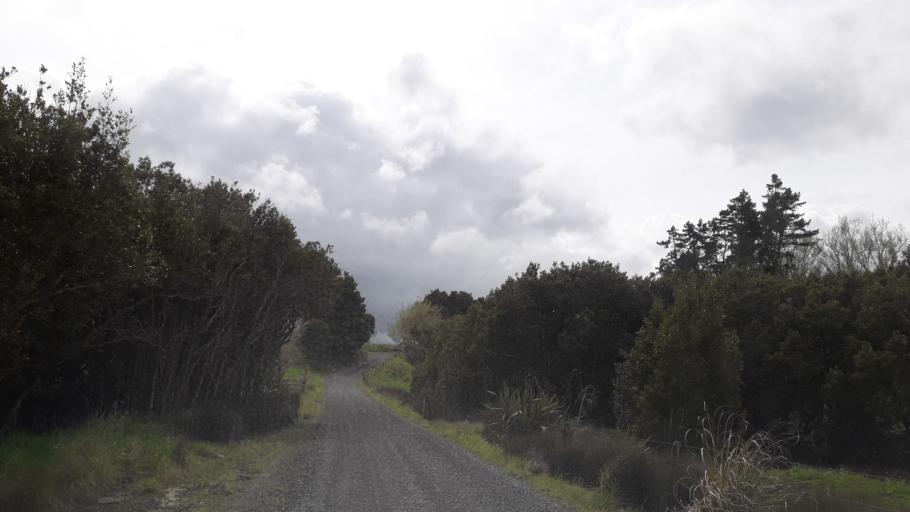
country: NZ
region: Northland
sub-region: Far North District
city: Waimate North
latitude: -35.3023
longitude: 173.5653
